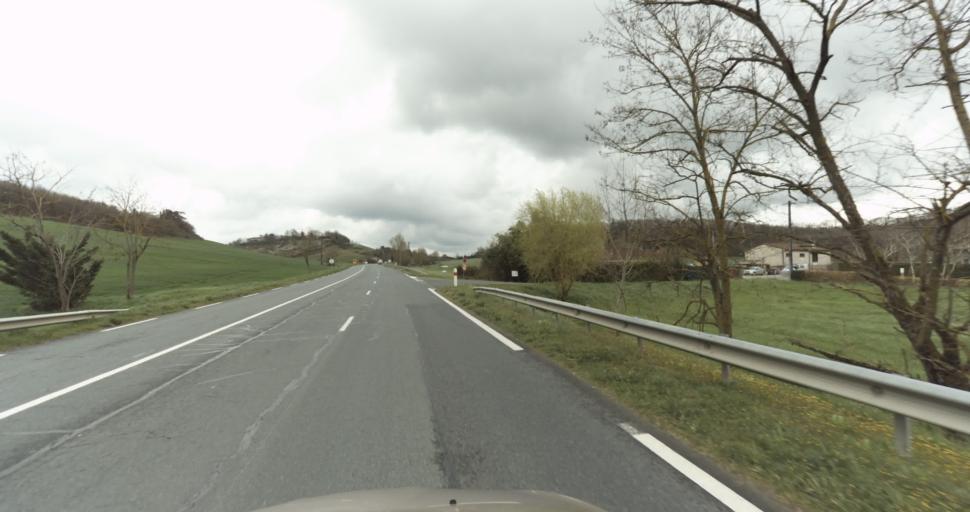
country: FR
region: Midi-Pyrenees
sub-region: Departement du Tarn
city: Puygouzon
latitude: 43.8716
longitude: 2.1816
